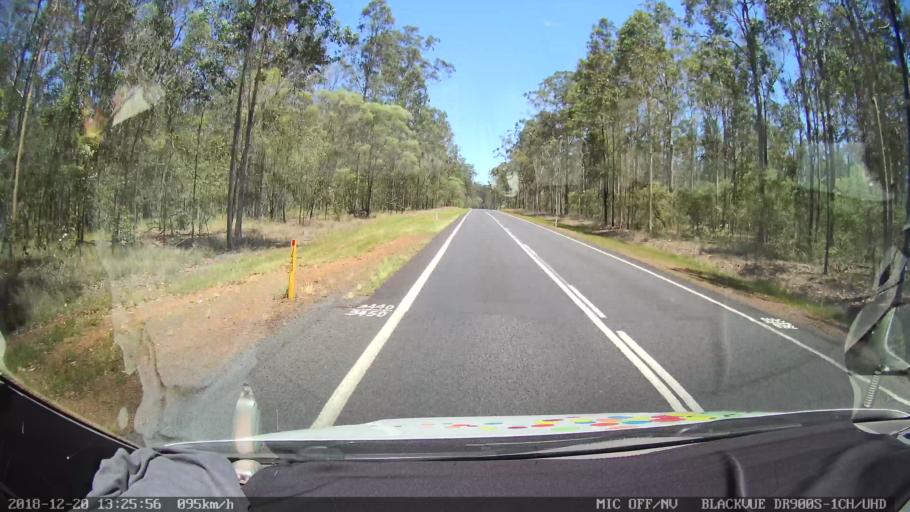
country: AU
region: New South Wales
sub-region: Richmond Valley
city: Casino
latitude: -29.1383
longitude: 152.9960
